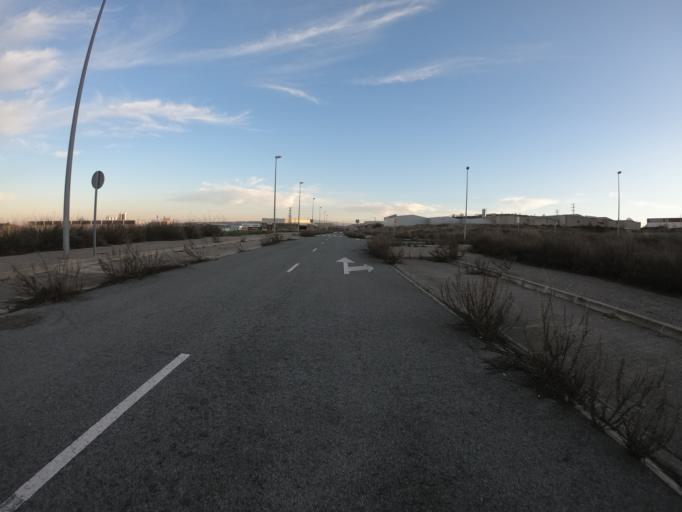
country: ES
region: Basque Country
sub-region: Provincia de Alava
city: Oyon
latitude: 42.4803
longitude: -2.4105
